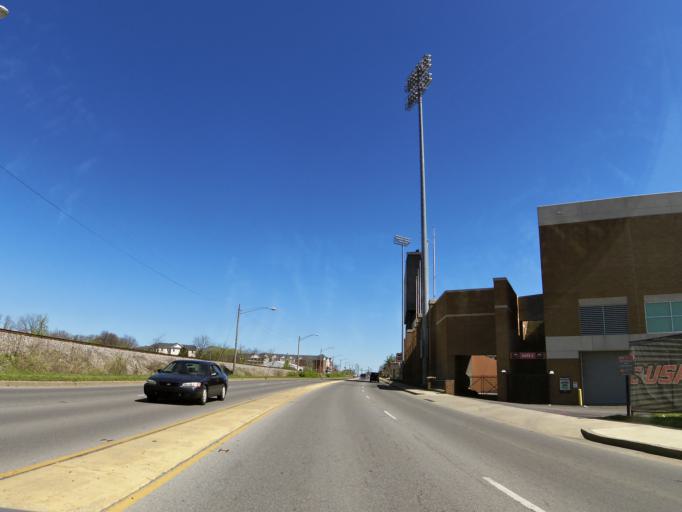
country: US
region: Kentucky
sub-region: Warren County
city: Bowling Green
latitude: 36.9846
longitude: -86.4610
